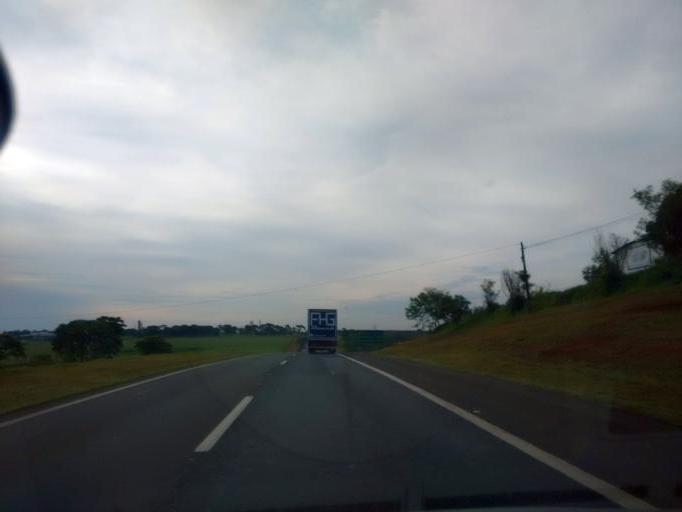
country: BR
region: Sao Paulo
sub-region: Araraquara
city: Araraquara
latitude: -21.7964
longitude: -48.2088
